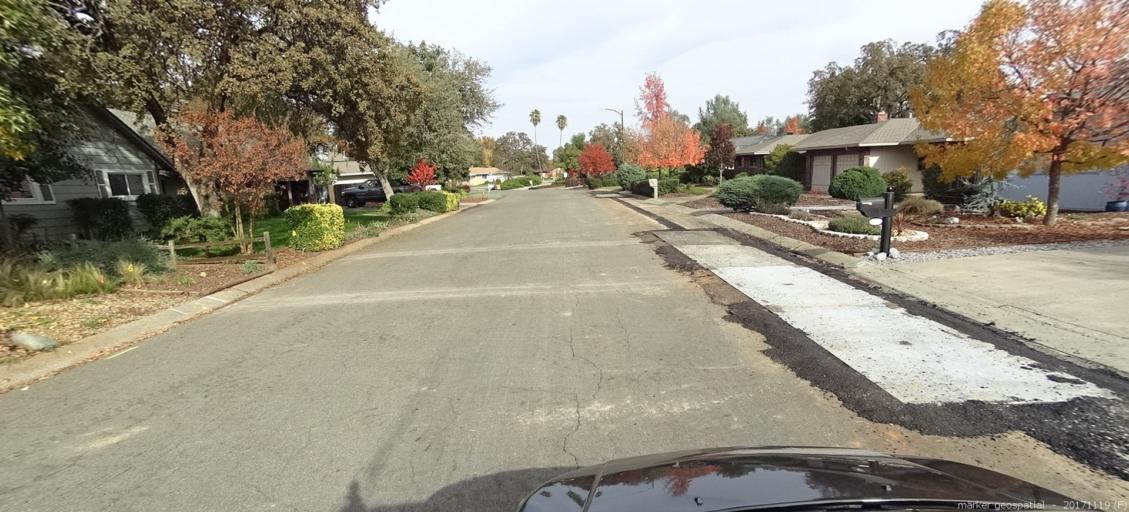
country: US
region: California
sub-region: Shasta County
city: Anderson
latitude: 40.4855
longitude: -122.3075
